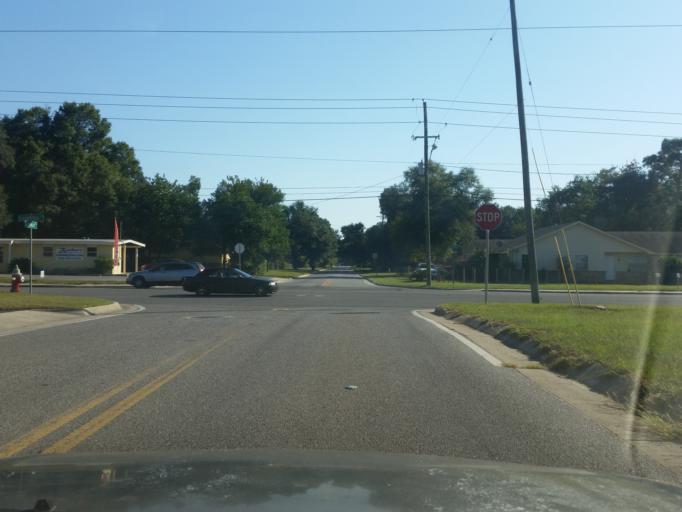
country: US
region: Florida
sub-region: Escambia County
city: Ferry Pass
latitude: 30.4958
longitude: -87.2008
